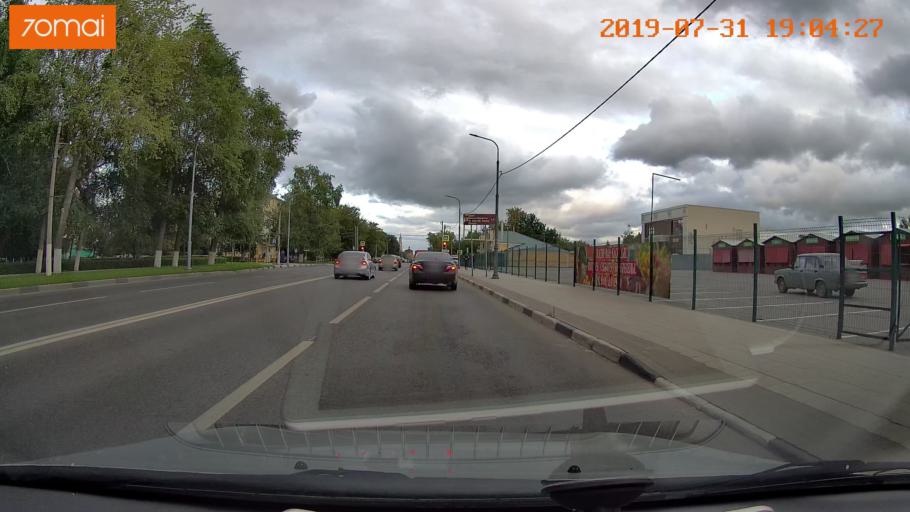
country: RU
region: Moskovskaya
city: Raduzhnyy
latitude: 55.1086
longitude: 38.7411
